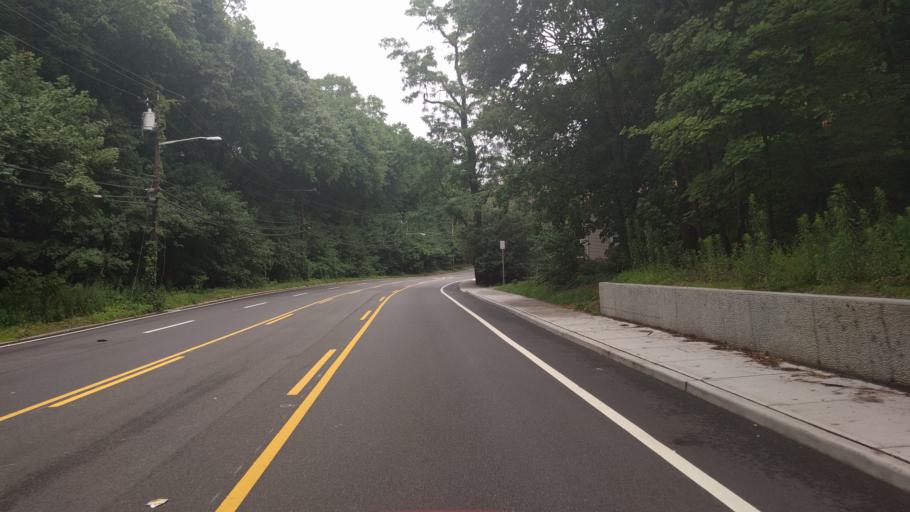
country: US
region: New York
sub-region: Suffolk County
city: Huntington
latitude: 40.8608
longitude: -73.4274
